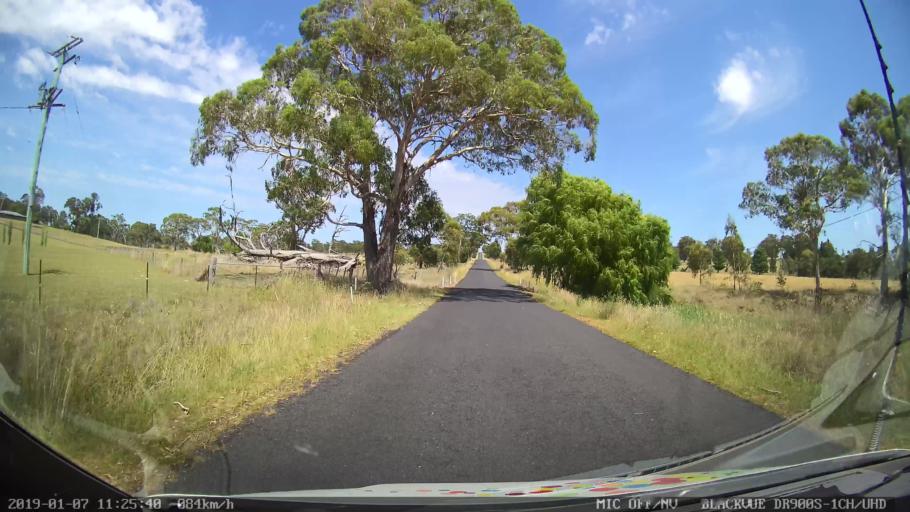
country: AU
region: New South Wales
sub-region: Armidale Dumaresq
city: Armidale
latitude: -30.4599
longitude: 151.5981
